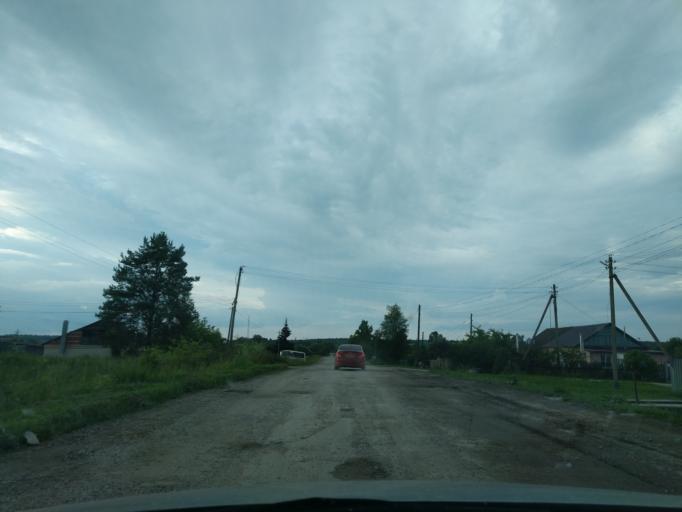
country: RU
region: Kaluga
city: Myatlevo
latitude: 54.7933
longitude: 35.7375
